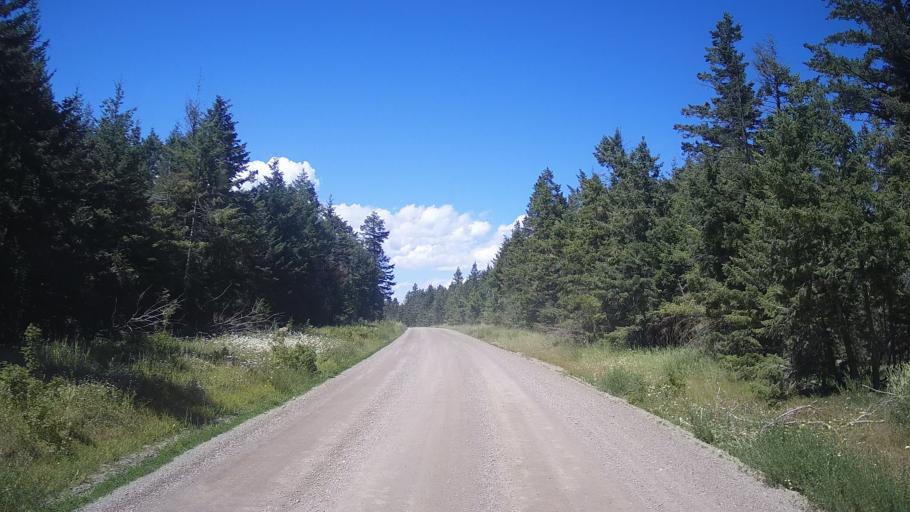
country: CA
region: British Columbia
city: Cache Creek
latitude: 51.1510
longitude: -121.5338
